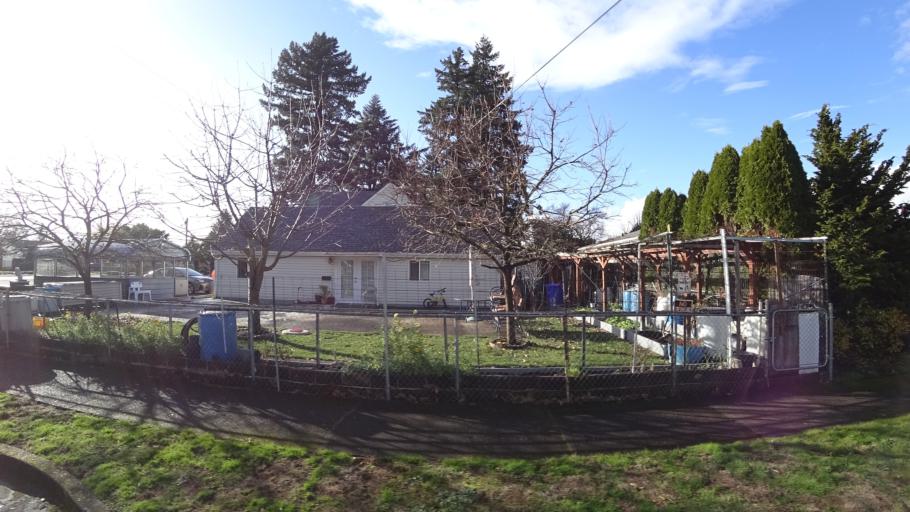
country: US
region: Oregon
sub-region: Multnomah County
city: Lents
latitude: 45.5267
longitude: -122.5495
